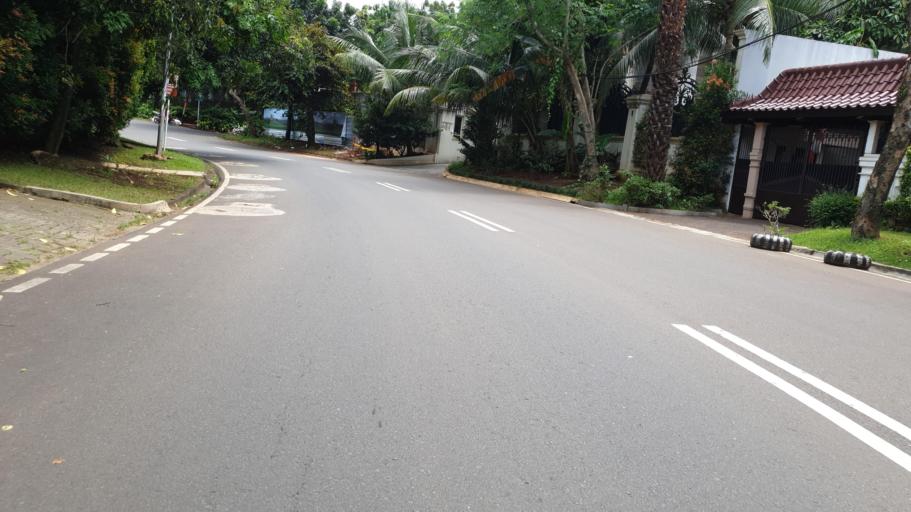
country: ID
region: Banten
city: South Tangerang
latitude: -6.2772
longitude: 106.7870
